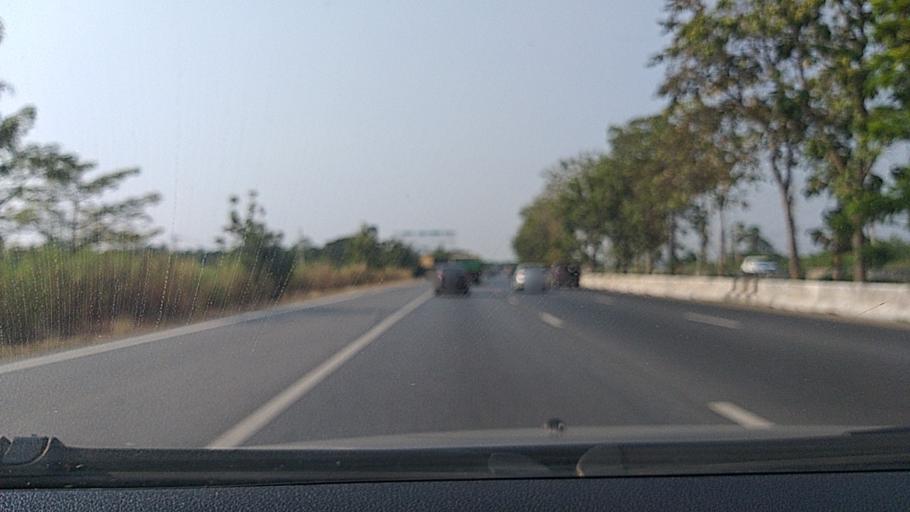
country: TH
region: Ang Thong
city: Chaiyo
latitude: 14.6924
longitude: 100.4592
